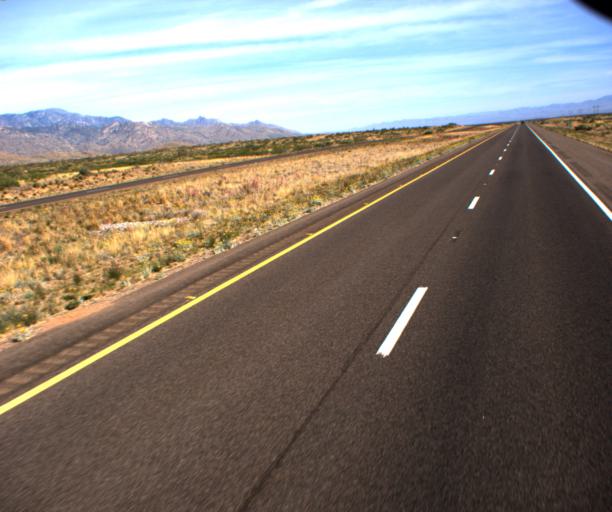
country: US
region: Arizona
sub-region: Graham County
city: Swift Trail Junction
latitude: 32.5626
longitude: -109.6794
